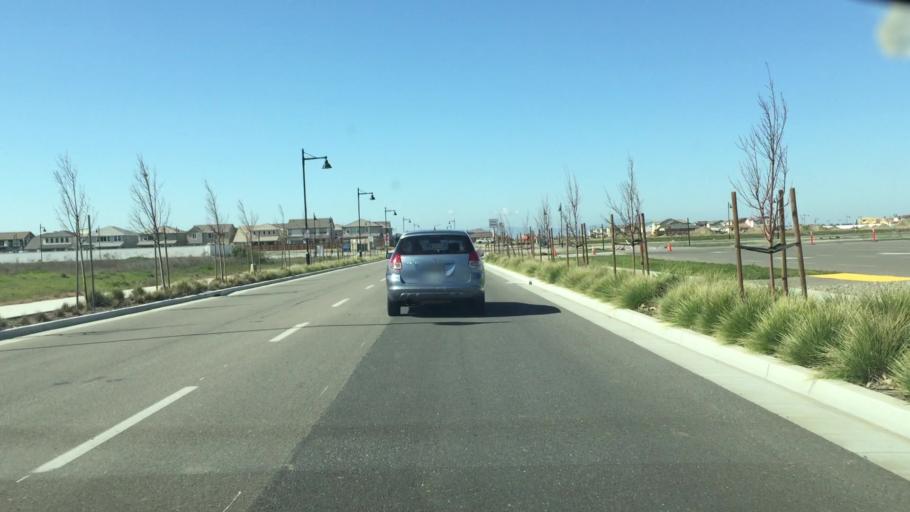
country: US
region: California
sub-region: San Joaquin County
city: Lathrop
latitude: 37.7988
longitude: -121.3207
